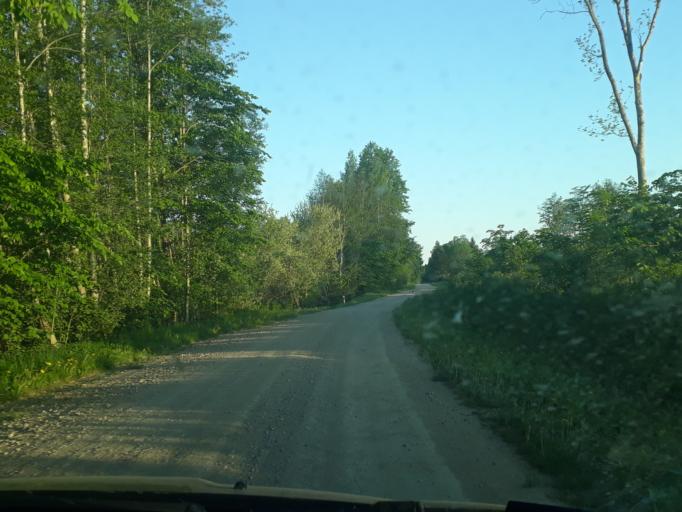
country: EE
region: Paernumaa
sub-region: Vaendra vald (alev)
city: Vandra
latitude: 58.5766
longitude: 24.9463
